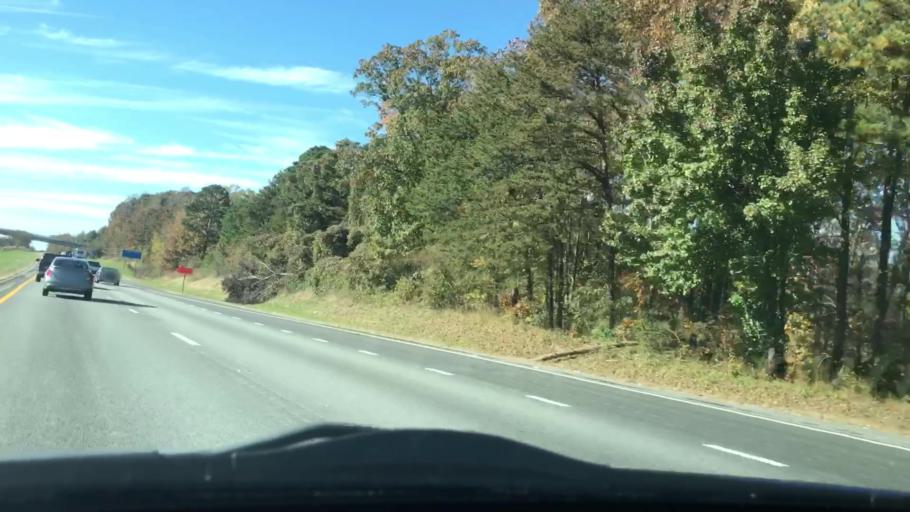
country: US
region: North Carolina
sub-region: Guilford County
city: High Point
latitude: 36.0061
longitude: -79.9982
